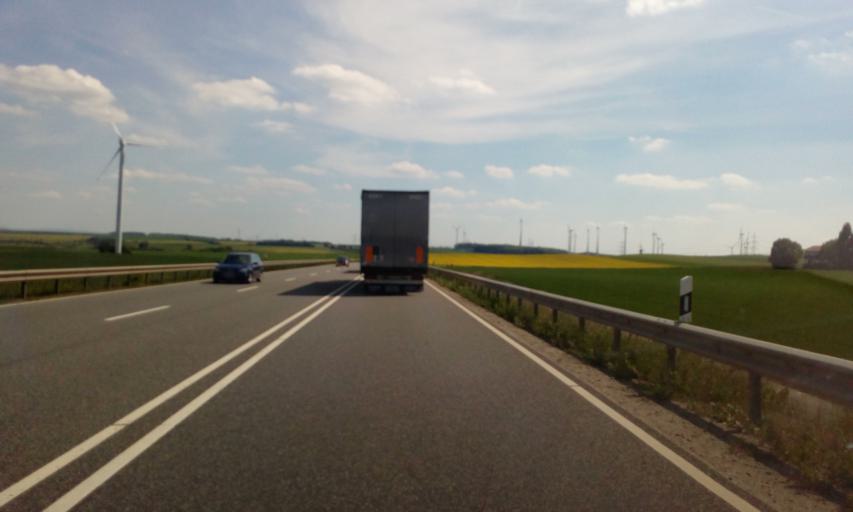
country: DE
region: Rheinland-Pfalz
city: Idesheim
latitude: 49.8708
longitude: 6.5447
